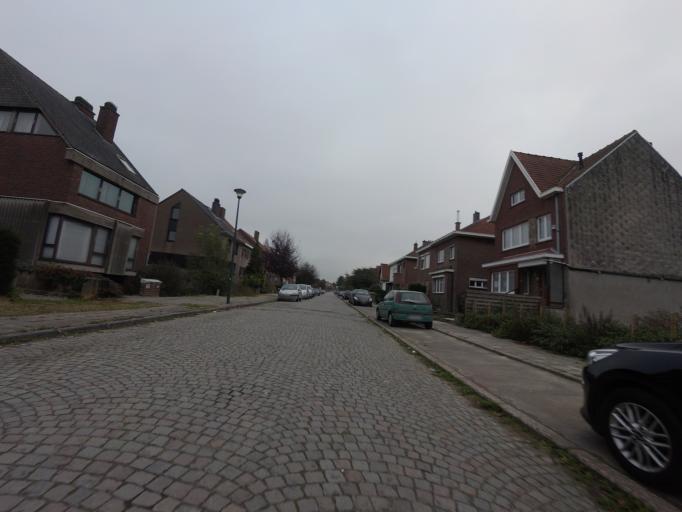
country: BE
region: Flanders
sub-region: Provincie Vlaams-Brabant
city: Diegem
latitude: 50.8688
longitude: 4.4356
